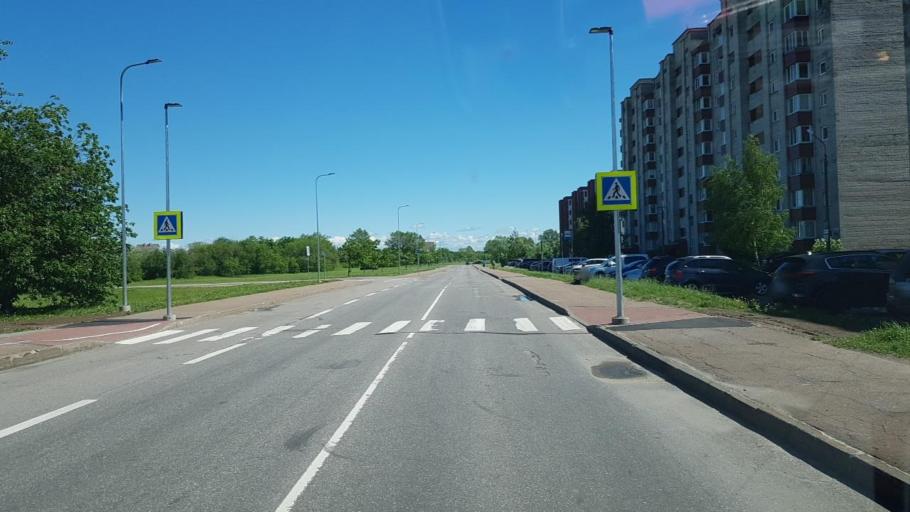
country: EE
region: Ida-Virumaa
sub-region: Narva linn
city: Narva
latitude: 59.3883
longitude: 28.1811
